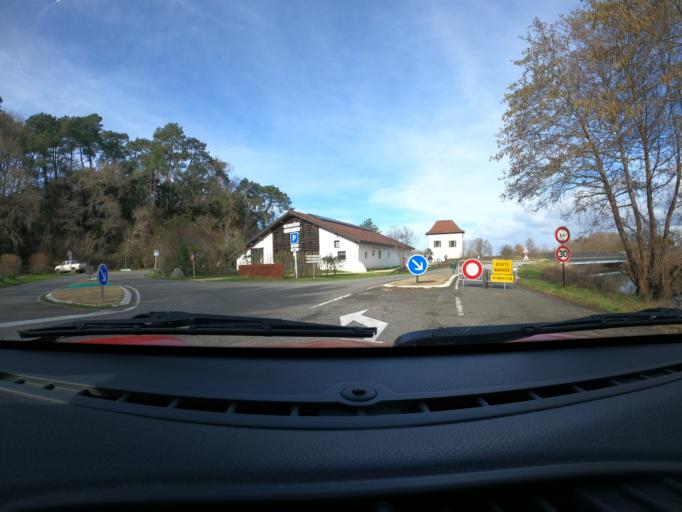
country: FR
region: Aquitaine
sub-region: Departement des Landes
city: Labenne
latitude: 43.5892
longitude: -1.4086
